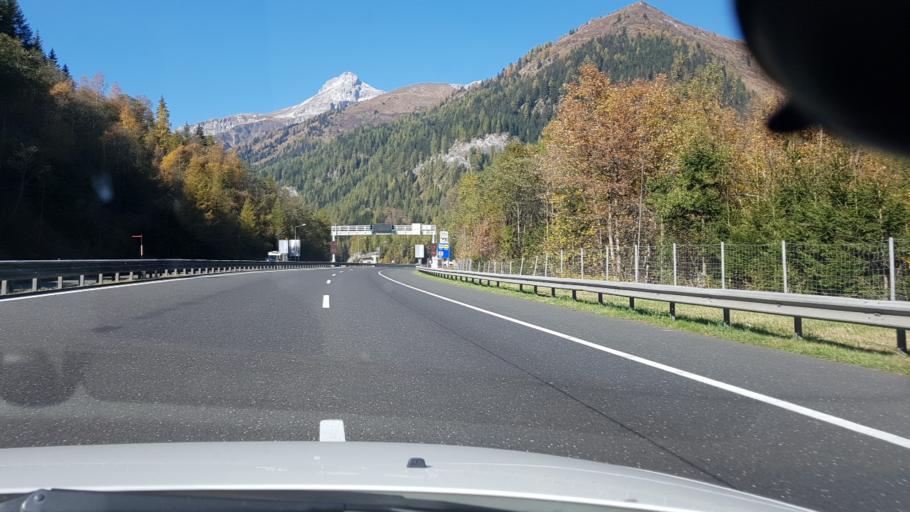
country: AT
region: Salzburg
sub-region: Politischer Bezirk Tamsweg
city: Zederhaus
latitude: 47.1789
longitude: 13.4424
